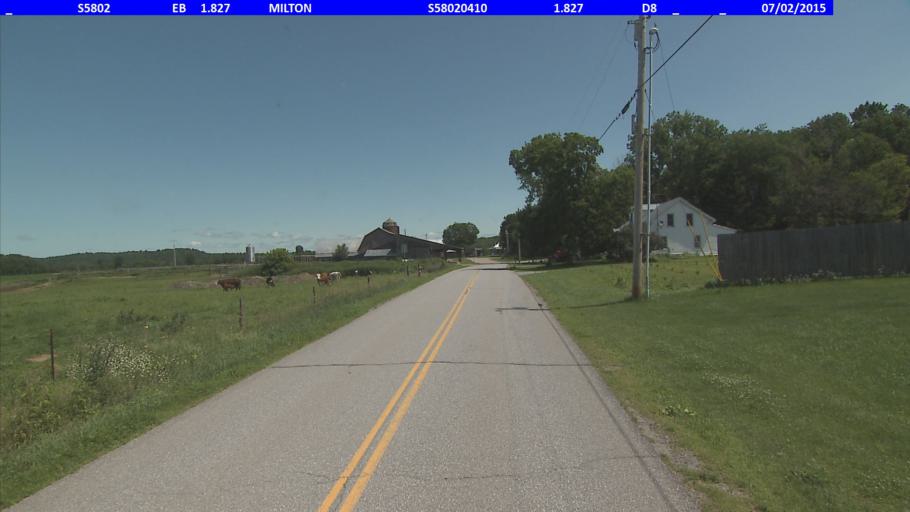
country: US
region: Vermont
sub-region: Chittenden County
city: Milton
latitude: 44.6306
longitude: -73.1903
